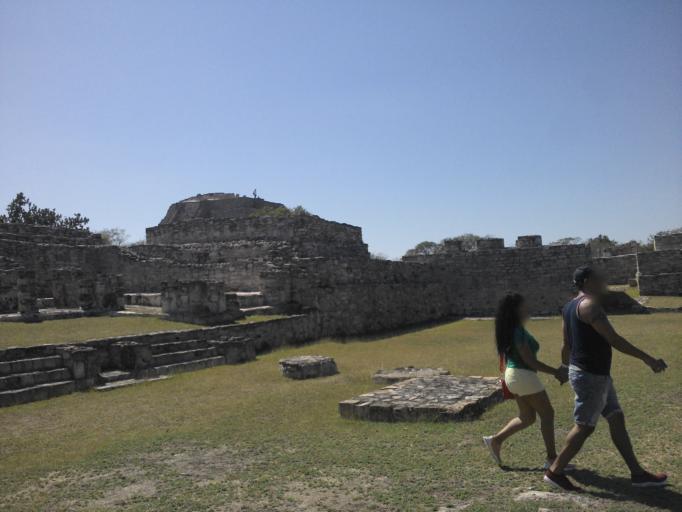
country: MX
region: Yucatan
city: Tekoh
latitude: 20.6297
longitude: -89.4603
